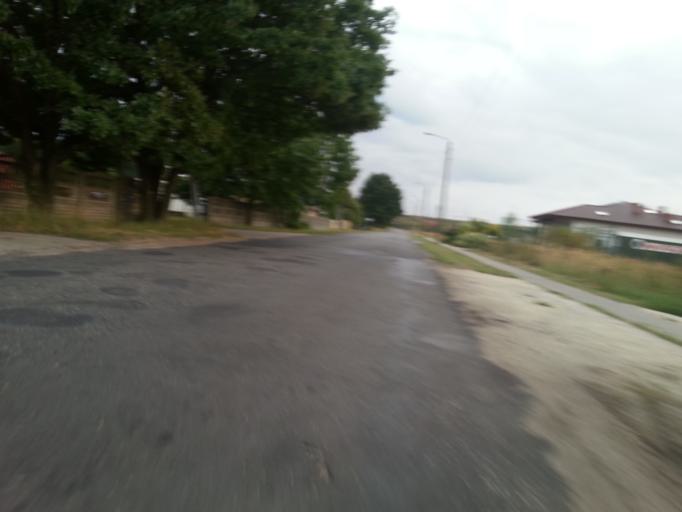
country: PL
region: Lower Silesian Voivodeship
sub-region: Powiat olesnicki
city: Twardogora
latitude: 51.3592
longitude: 17.4560
